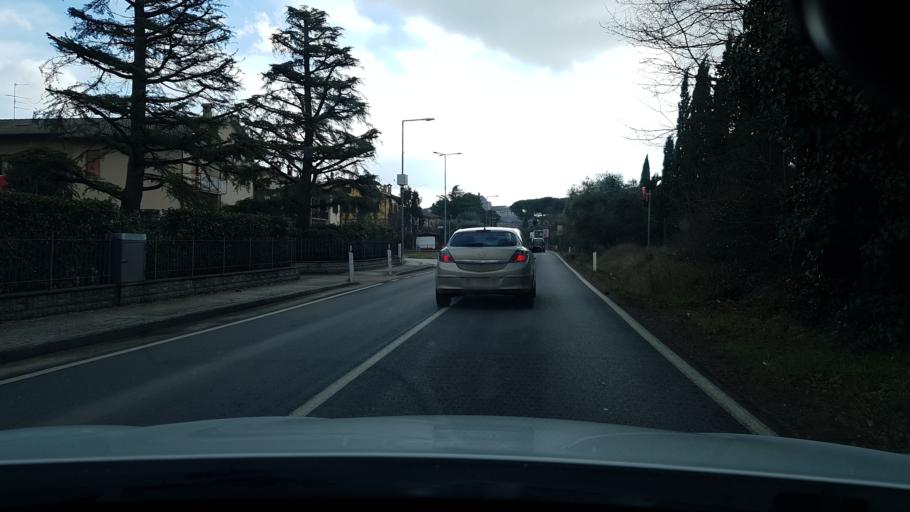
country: IT
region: Umbria
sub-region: Provincia di Perugia
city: Castiglione del Lago
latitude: 43.1323
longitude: 12.0387
